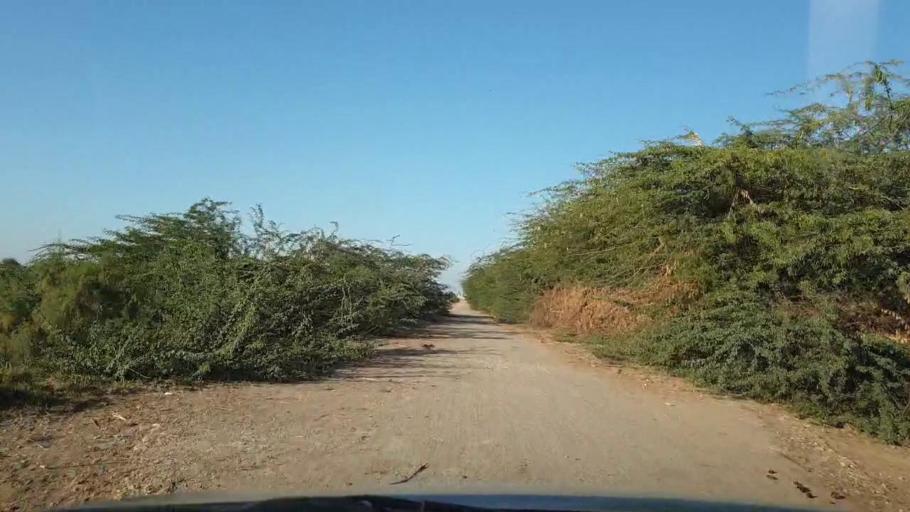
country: PK
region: Sindh
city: Jhol
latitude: 25.9023
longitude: 68.9250
